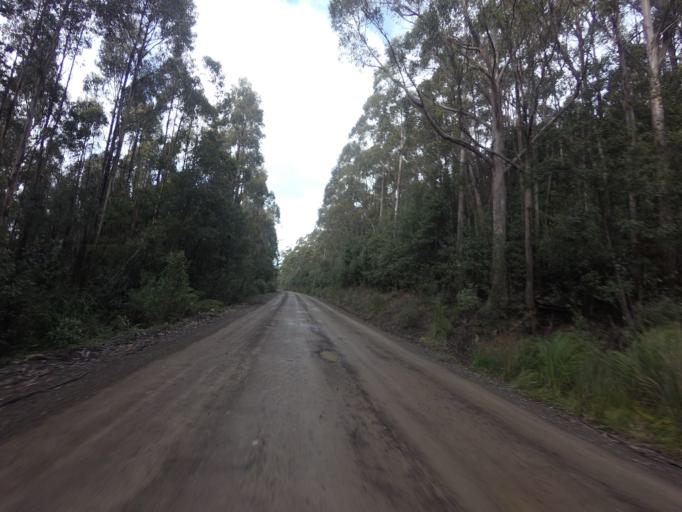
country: AU
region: Tasmania
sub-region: Huon Valley
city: Geeveston
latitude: -43.4743
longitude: 146.8922
